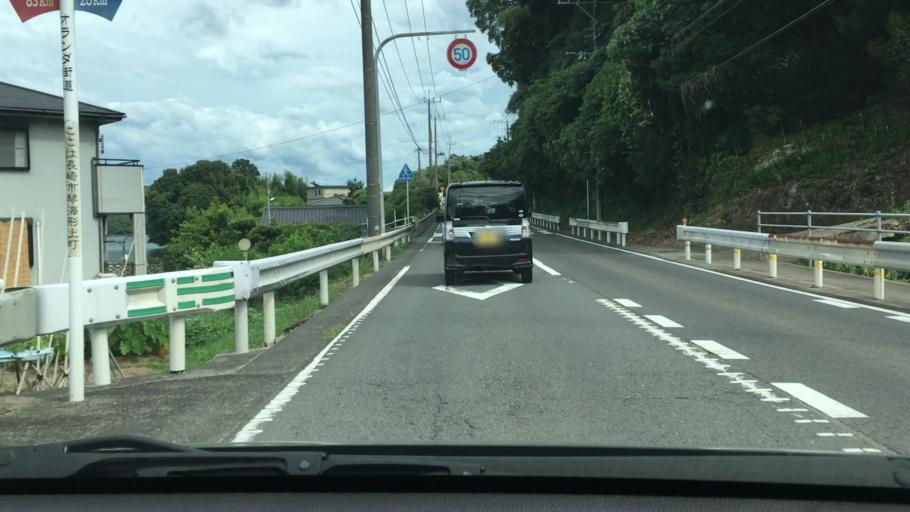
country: JP
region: Nagasaki
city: Togitsu
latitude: 32.9380
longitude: 129.7826
